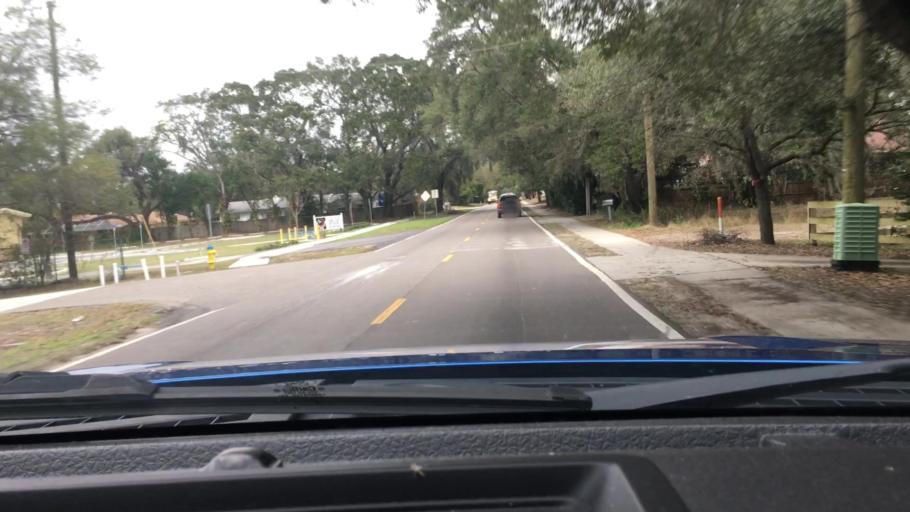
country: US
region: Florida
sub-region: Hillsborough County
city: Mango
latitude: 27.9642
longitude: -82.3104
